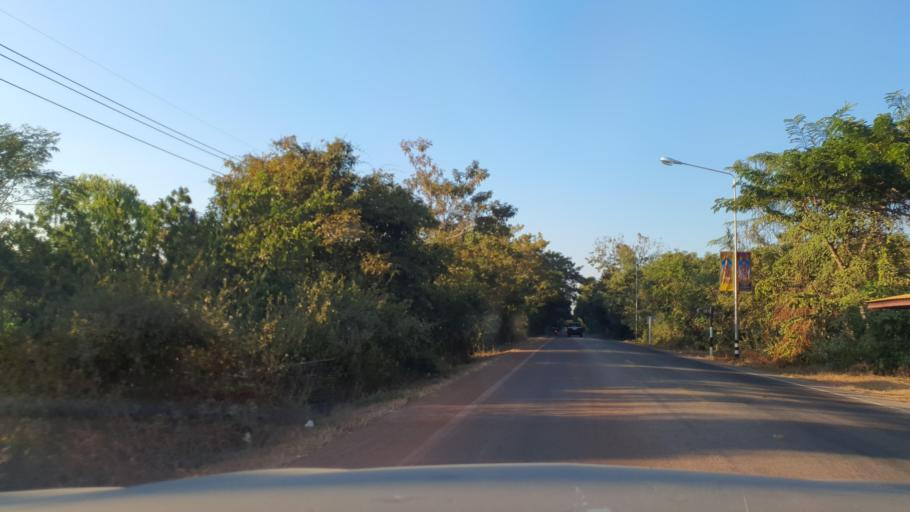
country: TH
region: Nakhon Phanom
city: Si Songkhram
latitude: 17.5612
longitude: 104.2369
